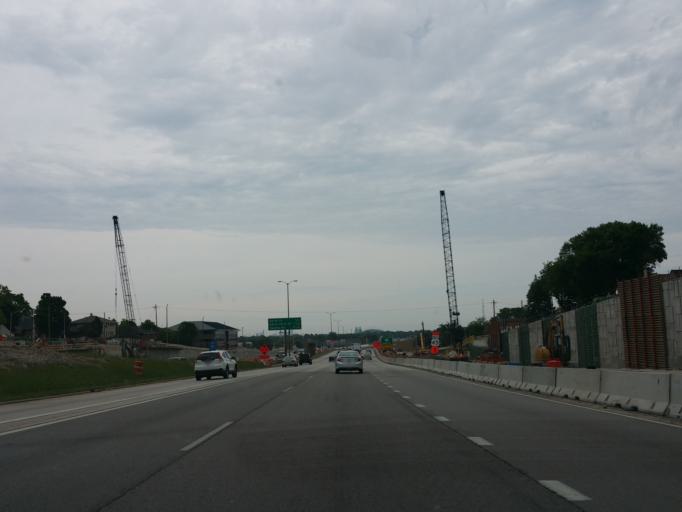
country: US
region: Wisconsin
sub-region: Milwaukee County
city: West Allis
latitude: 43.0278
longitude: -88.0298
